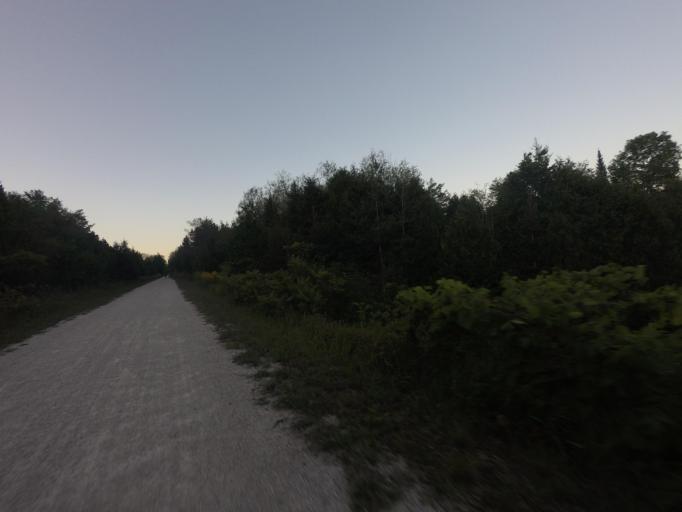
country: CA
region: Ontario
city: Orangeville
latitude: 43.9364
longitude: -79.8429
